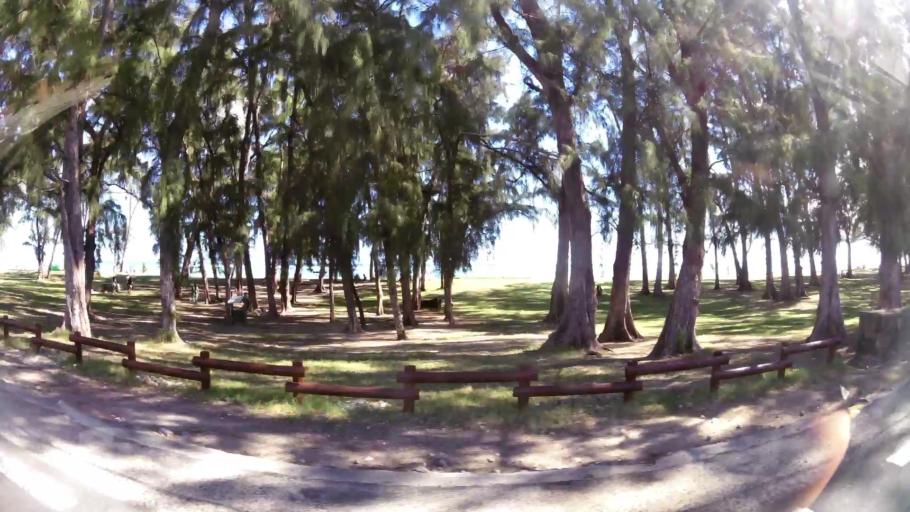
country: MU
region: Black River
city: Flic en Flac
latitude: -20.2832
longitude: 57.3649
